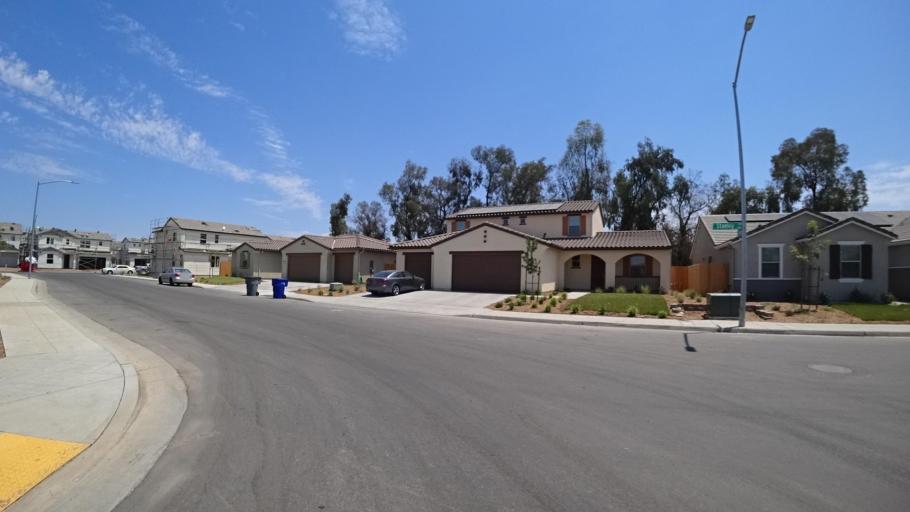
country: US
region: California
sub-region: Fresno County
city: Tarpey Village
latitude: 36.7752
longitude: -119.6568
